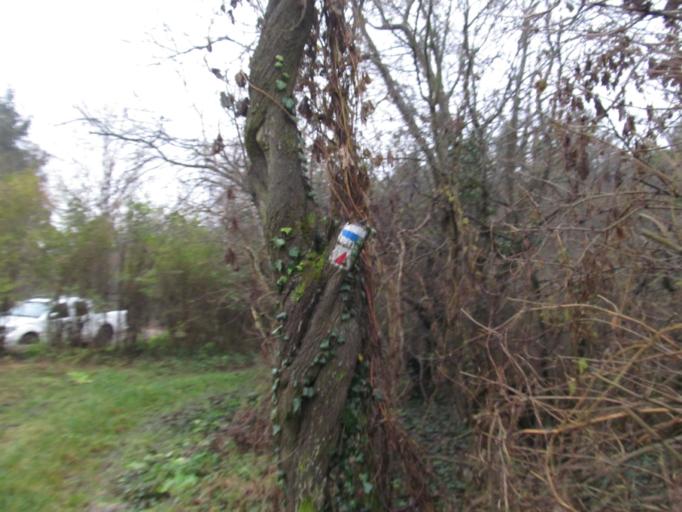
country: HU
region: Fejer
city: Bodajk
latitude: 47.2986
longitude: 18.2348
